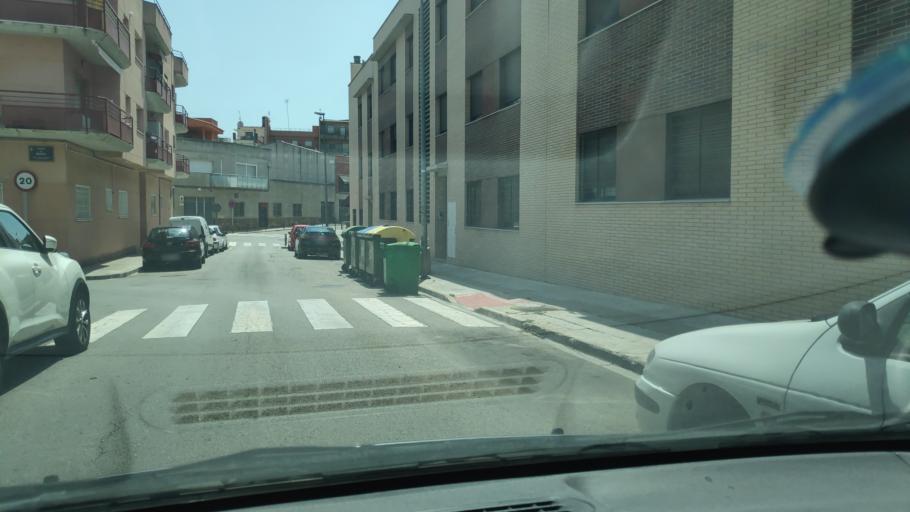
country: ES
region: Catalonia
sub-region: Provincia de Barcelona
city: Terrassa
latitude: 41.5624
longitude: 2.0386
